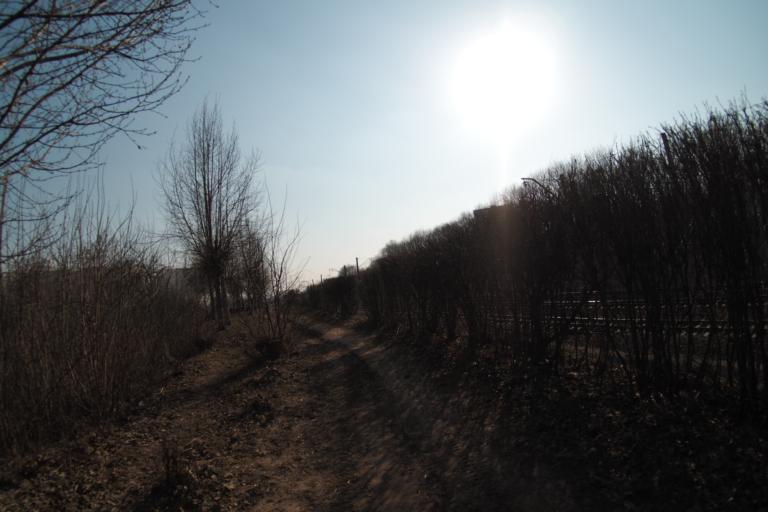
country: RU
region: Moskovskaya
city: Kastanayevo
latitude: 55.7109
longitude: 37.4919
